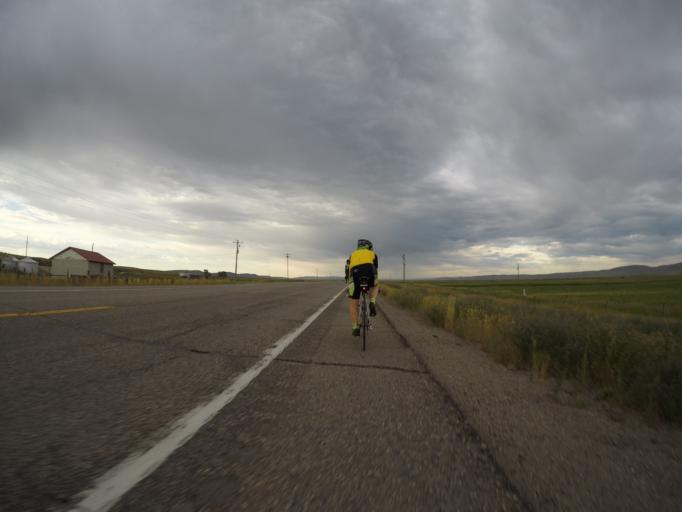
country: US
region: Utah
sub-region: Rich County
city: Randolph
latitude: 41.9537
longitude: -110.9488
